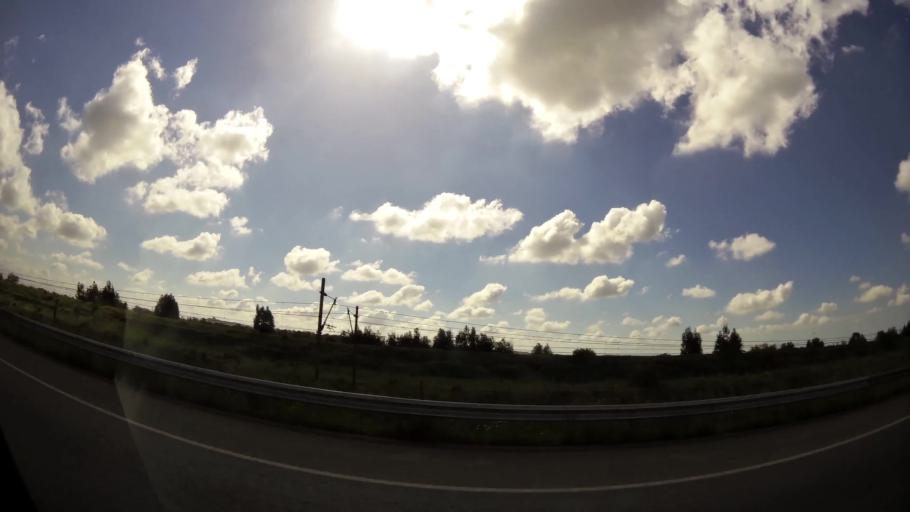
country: MA
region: Grand Casablanca
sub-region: Nouaceur
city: Bouskoura
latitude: 33.4295
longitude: -7.6277
